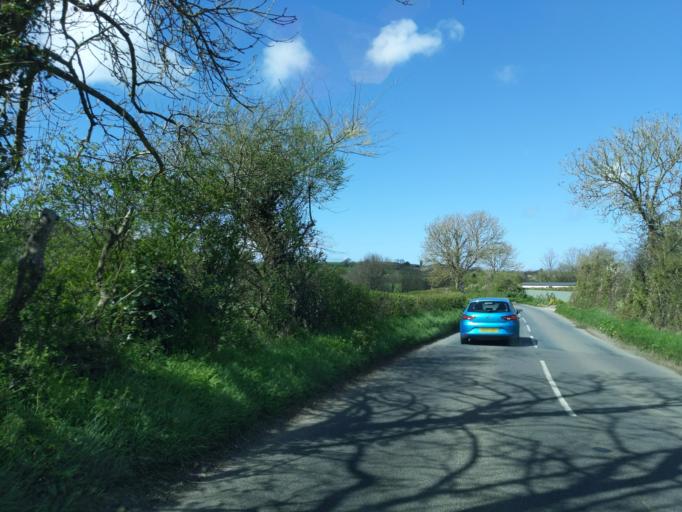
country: GB
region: England
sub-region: Cornwall
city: Wadebridge
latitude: 50.5400
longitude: -4.8555
